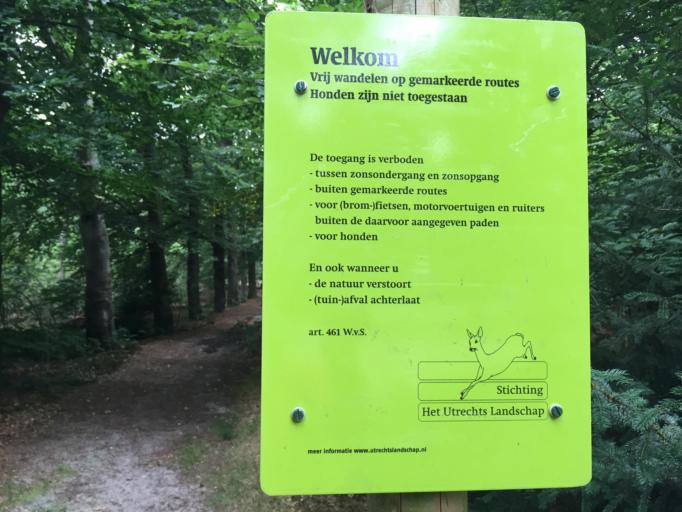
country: NL
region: Utrecht
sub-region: Gemeente Zeist
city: Zeist
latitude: 52.1471
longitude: 5.2369
